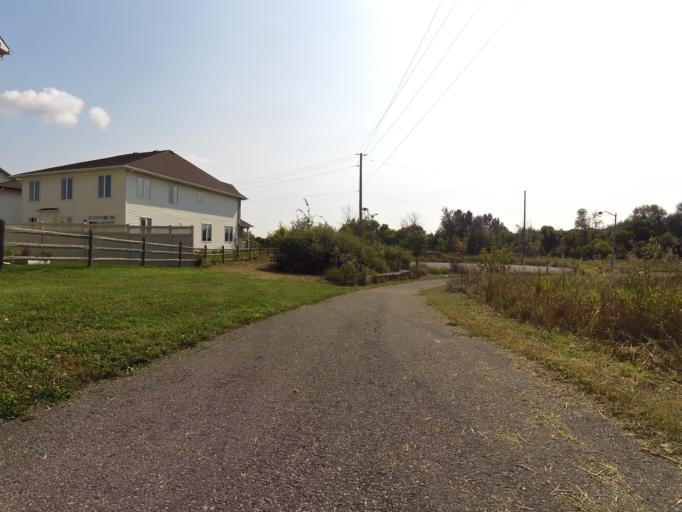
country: CA
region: Ontario
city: Bells Corners
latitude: 45.2654
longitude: -75.7313
